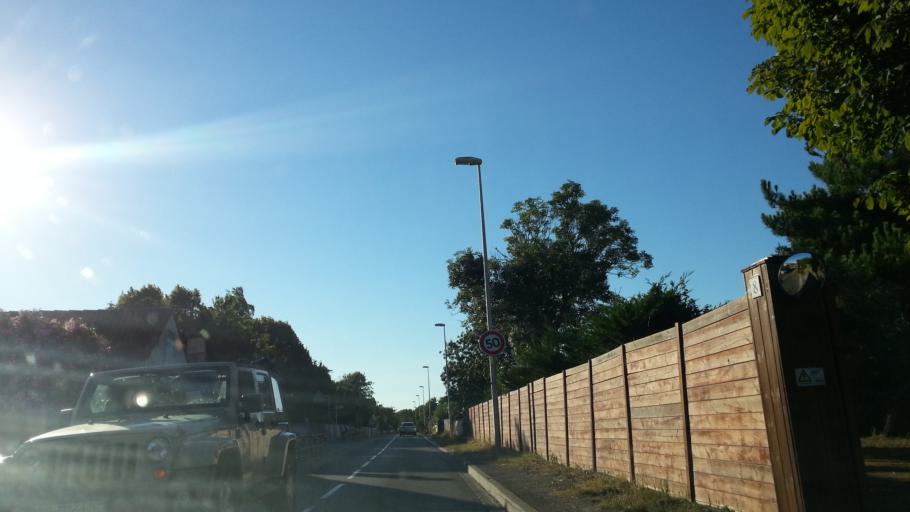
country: FR
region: Poitou-Charentes
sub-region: Departement de la Charente-Maritime
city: Dolus-d'Oleron
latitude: 45.8987
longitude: -1.2874
